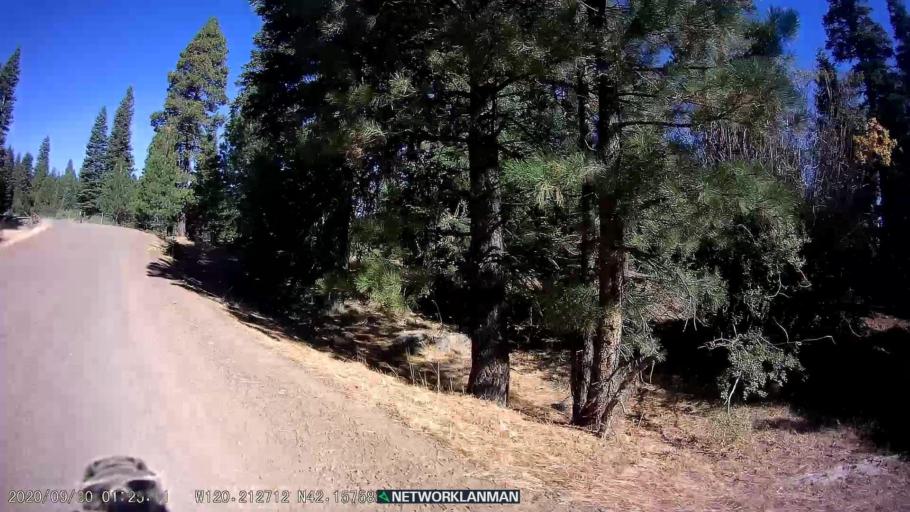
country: US
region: Oregon
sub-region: Lake County
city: Lakeview
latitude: 42.1580
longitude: -120.2169
